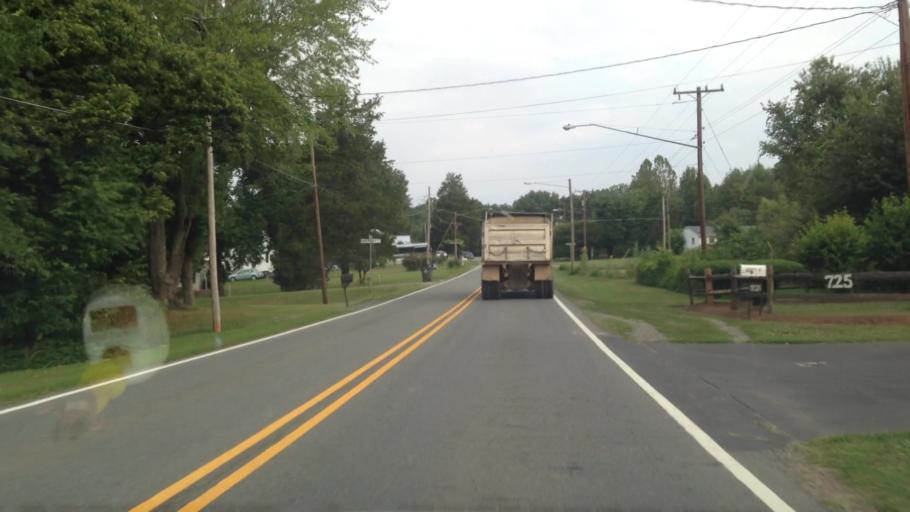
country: US
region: North Carolina
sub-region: Forsyth County
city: Rural Hall
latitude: 36.1926
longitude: -80.2477
